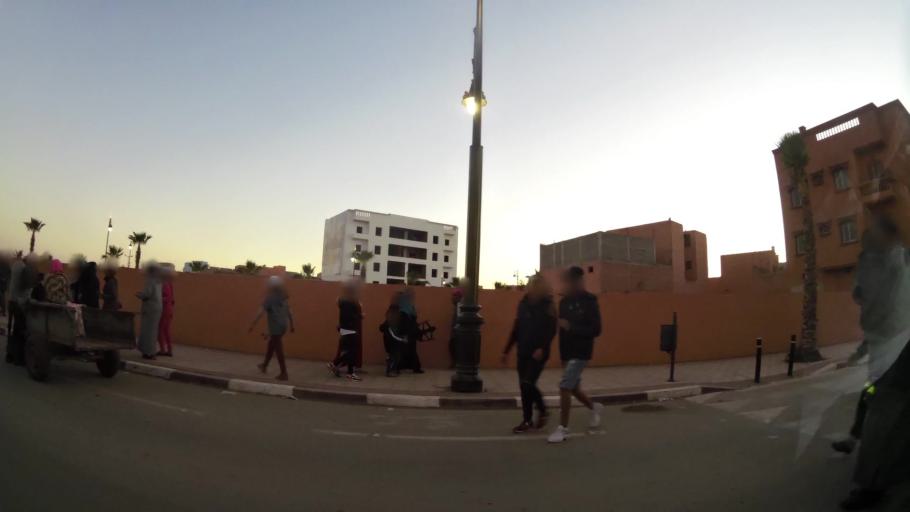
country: MA
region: Marrakech-Tensift-Al Haouz
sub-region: Kelaa-Des-Sraghna
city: Sidi Bou Othmane
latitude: 32.2278
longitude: -7.9458
